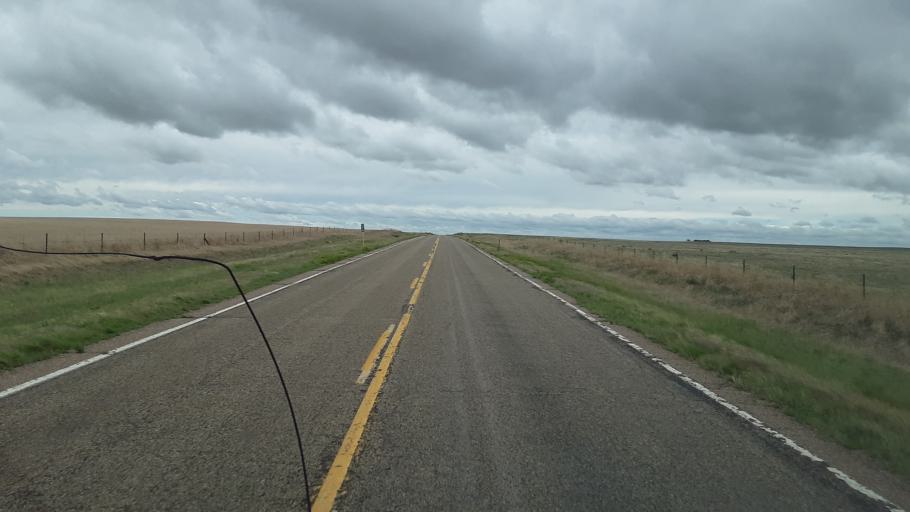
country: US
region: Colorado
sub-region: Lincoln County
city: Hugo
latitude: 38.8513
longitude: -103.6355
